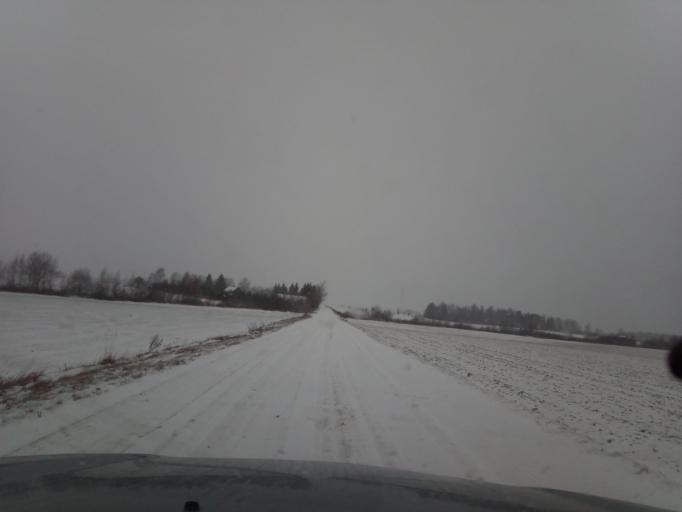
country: LT
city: Ramygala
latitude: 55.5623
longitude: 24.3536
